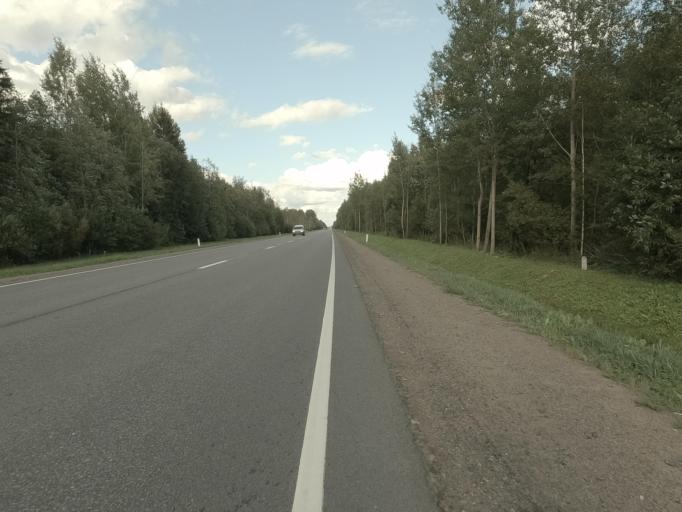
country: RU
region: Leningrad
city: Mga
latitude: 59.6816
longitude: 30.9514
